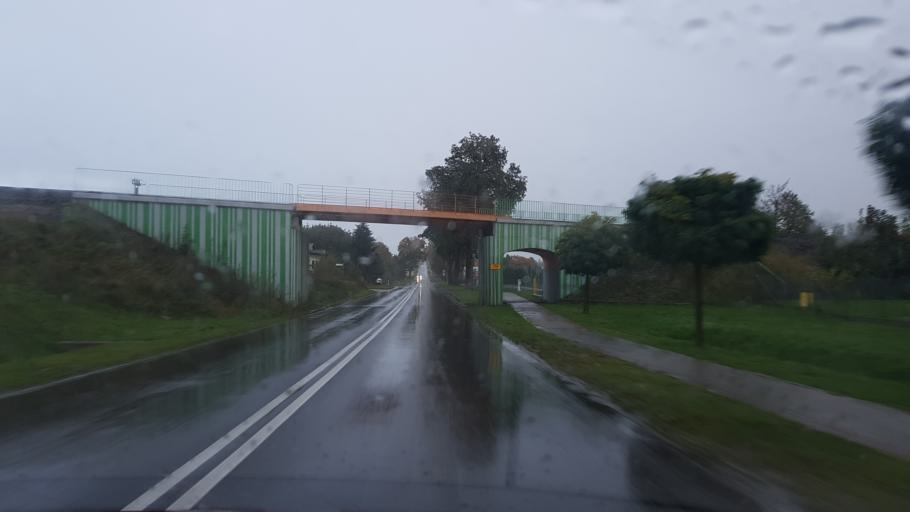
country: PL
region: Greater Poland Voivodeship
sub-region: Powiat pilski
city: Szydlowo
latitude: 53.1619
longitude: 16.6196
